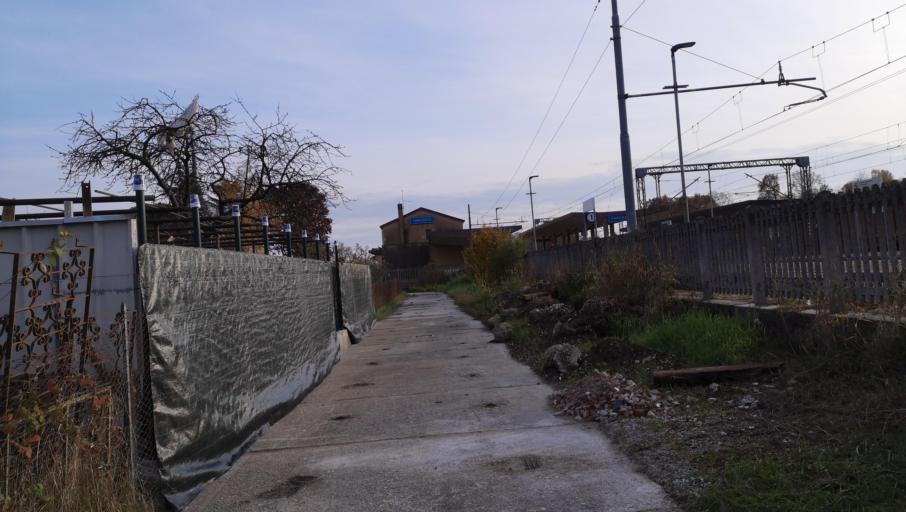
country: IT
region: Friuli Venezia Giulia
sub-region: Provincia di Udine
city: Magnano in Riviera
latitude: 46.2102
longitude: 13.1959
